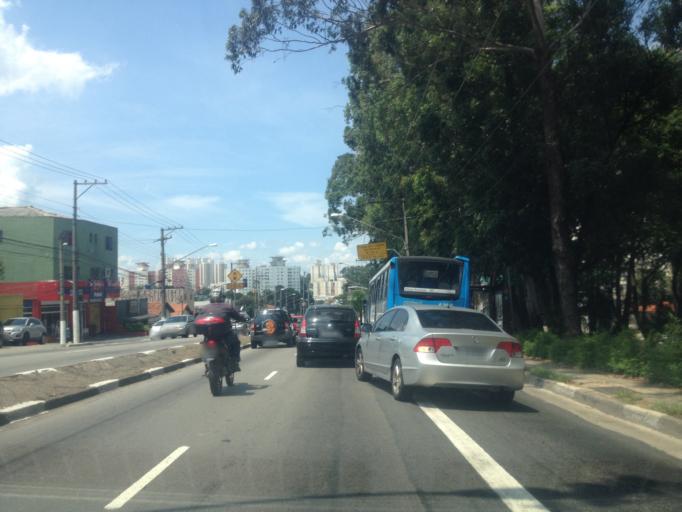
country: BR
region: Sao Paulo
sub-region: Diadema
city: Diadema
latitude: -23.6556
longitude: -46.6798
